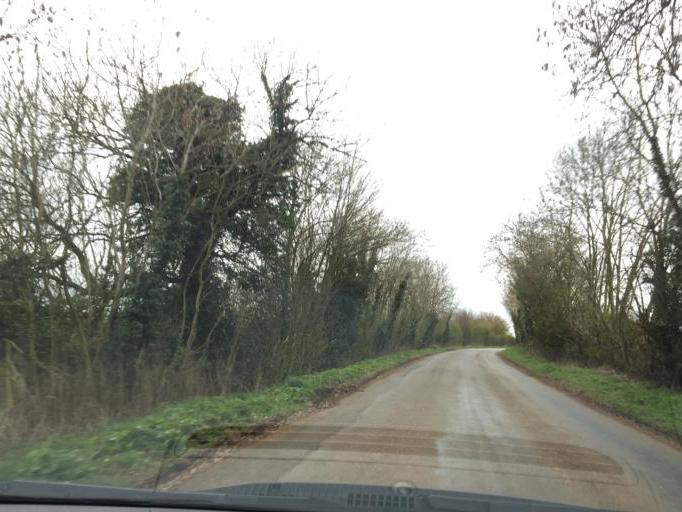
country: GB
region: England
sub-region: Oxfordshire
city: Hanwell
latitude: 52.1032
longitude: -1.4183
